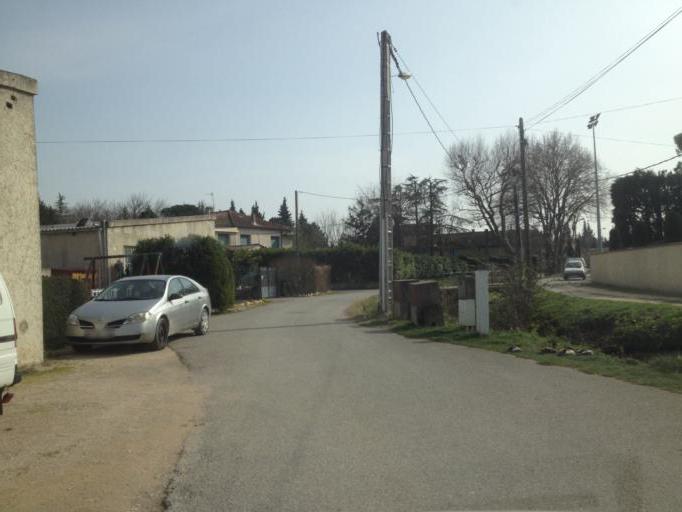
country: FR
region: Provence-Alpes-Cote d'Azur
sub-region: Departement du Vaucluse
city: Courthezon
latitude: 44.0922
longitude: 4.8856
